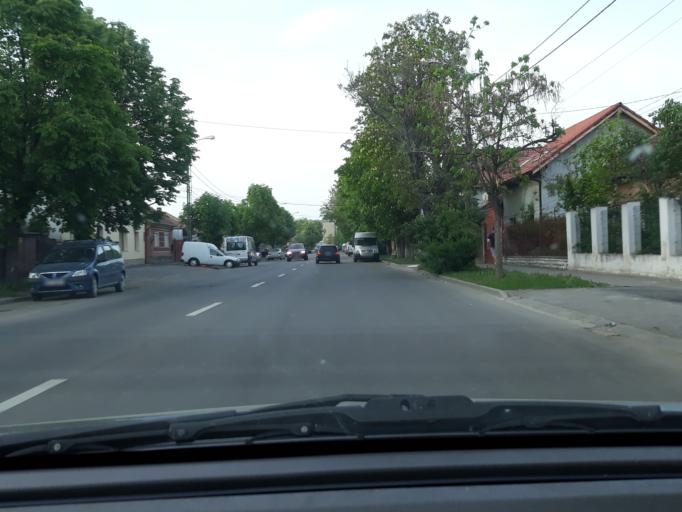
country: RO
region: Bihor
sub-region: Comuna Biharea
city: Oradea
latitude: 47.0405
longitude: 21.9552
